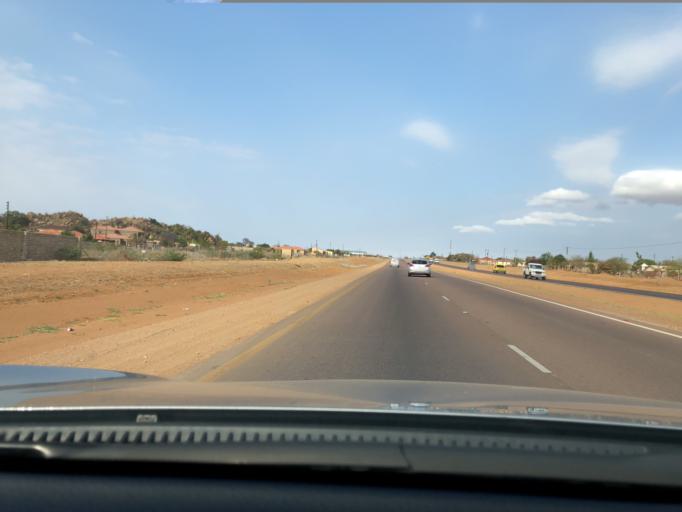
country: ZA
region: Limpopo
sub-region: Capricorn District Municipality
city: Mankoeng
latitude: -23.8913
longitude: 29.6566
